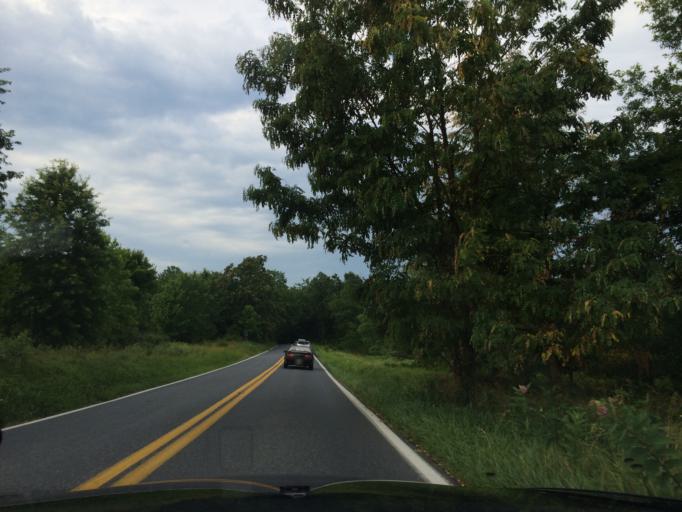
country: US
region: Maryland
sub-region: Montgomery County
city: Clarksburg
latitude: 39.2746
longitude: -77.2765
